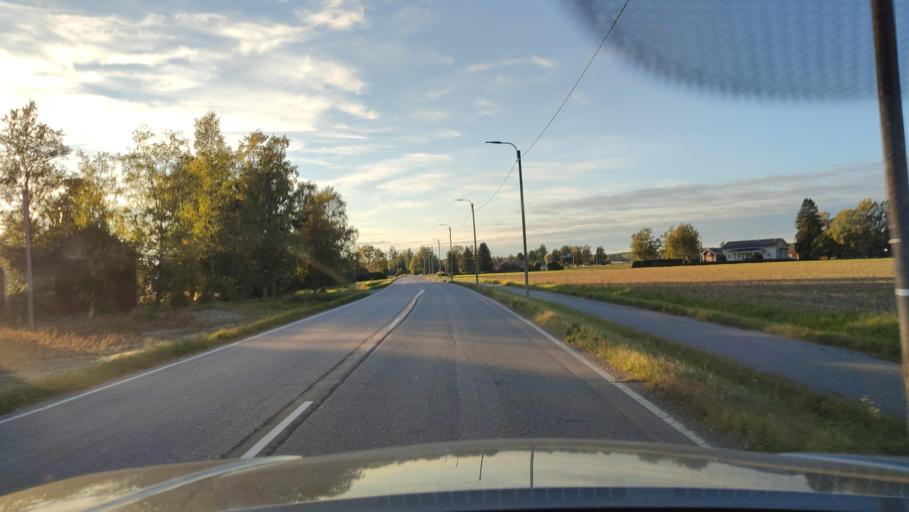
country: FI
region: Ostrobothnia
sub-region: Sydosterbotten
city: Kristinestad
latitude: 62.2573
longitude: 21.4967
